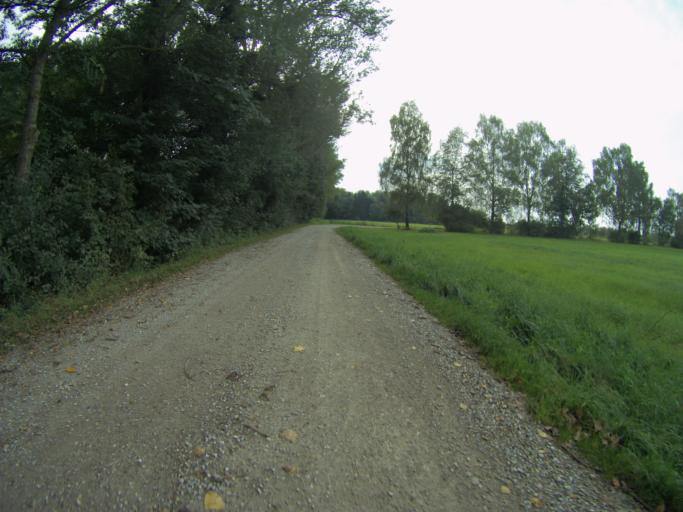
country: DE
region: Bavaria
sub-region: Upper Bavaria
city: Marzling
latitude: 48.3844
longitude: 11.8331
